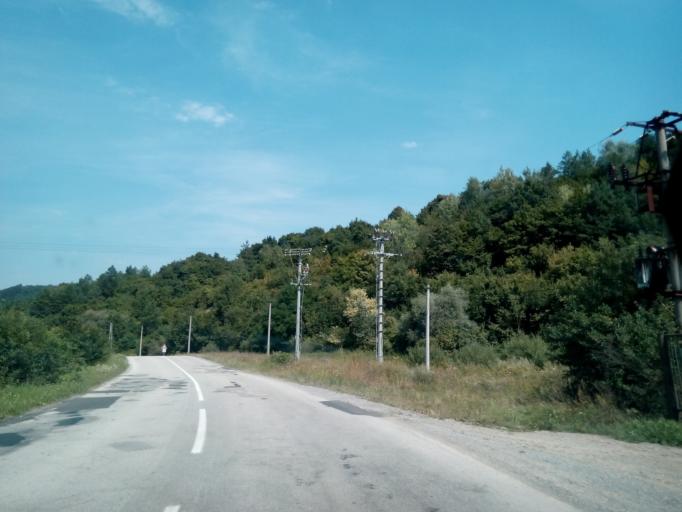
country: SK
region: Kosicky
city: Kosice
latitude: 48.8115
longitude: 21.2359
